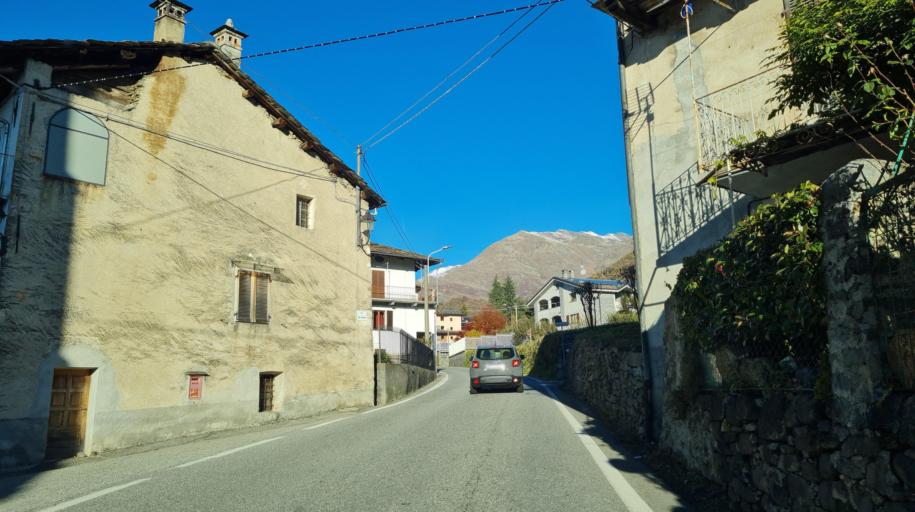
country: IT
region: Piedmont
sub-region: Provincia di Torino
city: Meugliano
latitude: 45.4903
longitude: 7.7798
